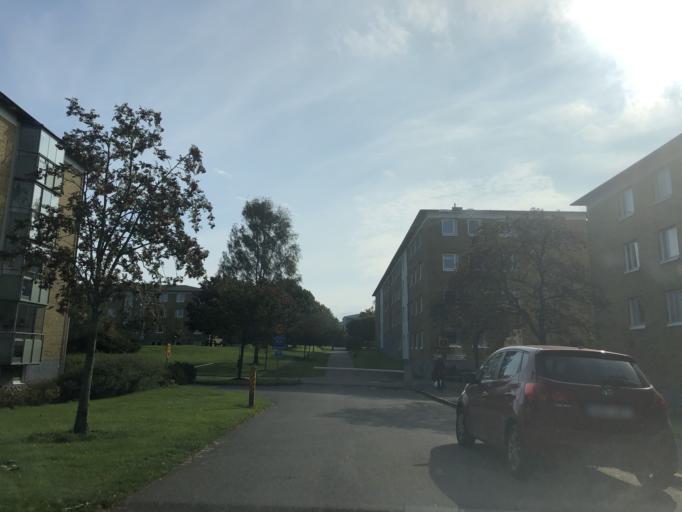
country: SE
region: Vaestra Goetaland
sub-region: Goteborg
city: Majorna
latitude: 57.6487
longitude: 11.8969
